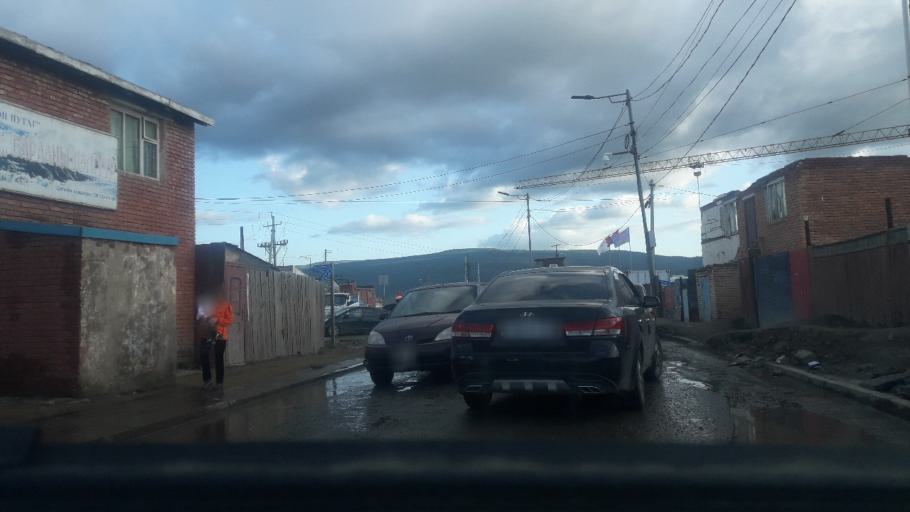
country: MN
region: Ulaanbaatar
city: Ulaanbaatar
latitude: 47.9218
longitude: 106.9953
